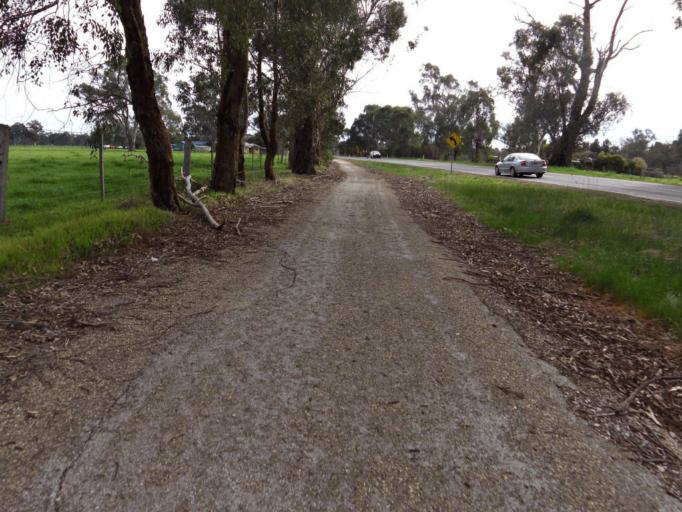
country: AU
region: Victoria
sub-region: Wangaratta
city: Wangaratta
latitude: -36.4008
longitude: 146.3469
